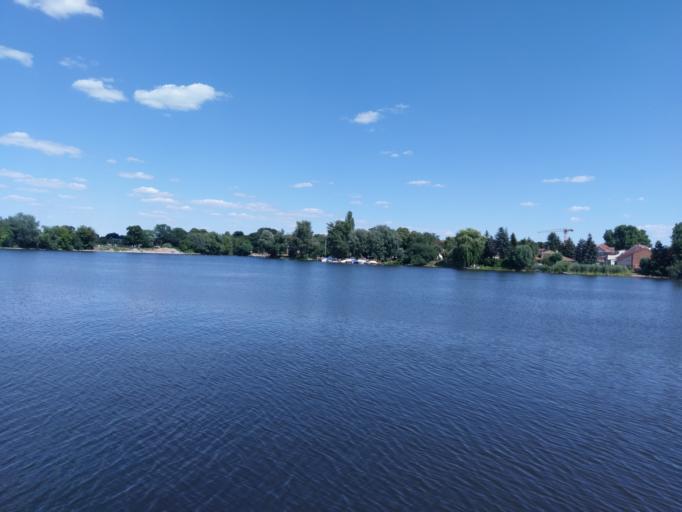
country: DE
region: Brandenburg
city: Brandenburg an der Havel
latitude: 52.4211
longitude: 12.5644
